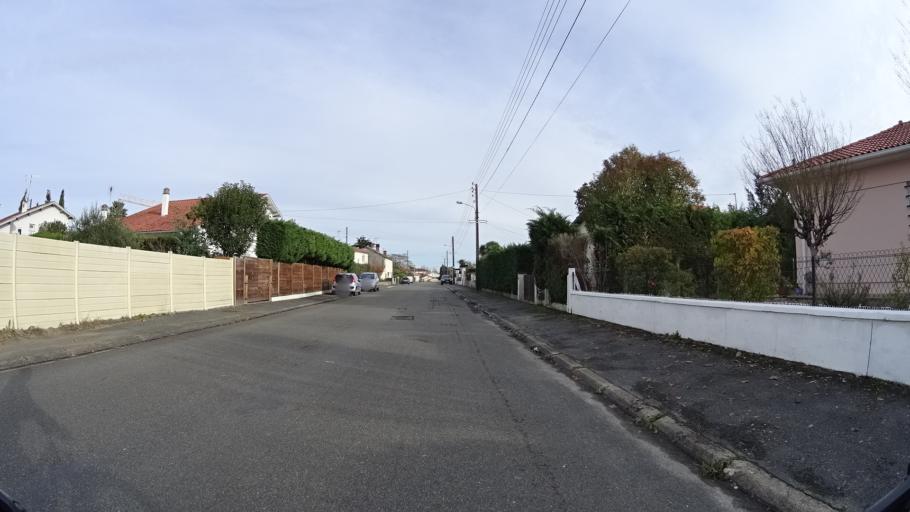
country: FR
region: Aquitaine
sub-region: Departement des Landes
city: Saint-Paul-les-Dax
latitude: 43.7311
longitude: -1.0545
